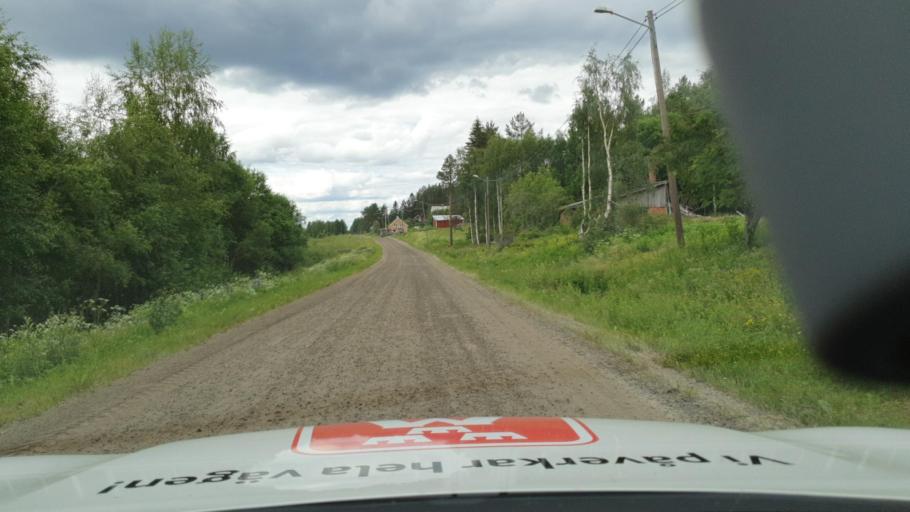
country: SE
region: Vaesterbotten
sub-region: Bjurholms Kommun
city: Bjurholm
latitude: 63.8171
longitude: 19.0286
